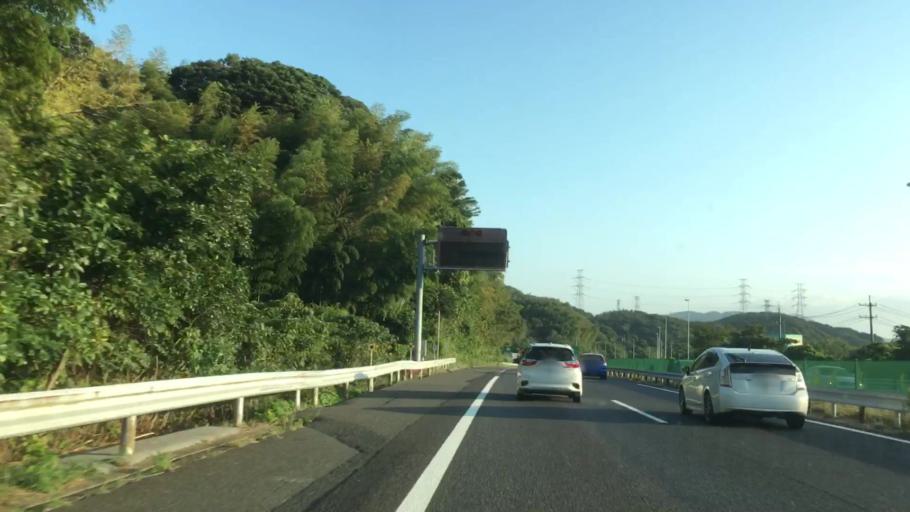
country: JP
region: Yamaguchi
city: Shimonoseki
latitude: 33.9837
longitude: 130.9519
